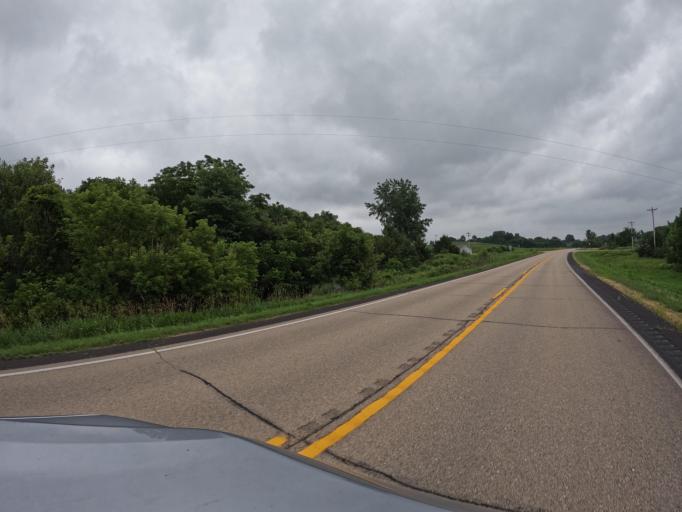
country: US
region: Illinois
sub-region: Carroll County
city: Savanna
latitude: 42.0194
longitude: -90.1823
